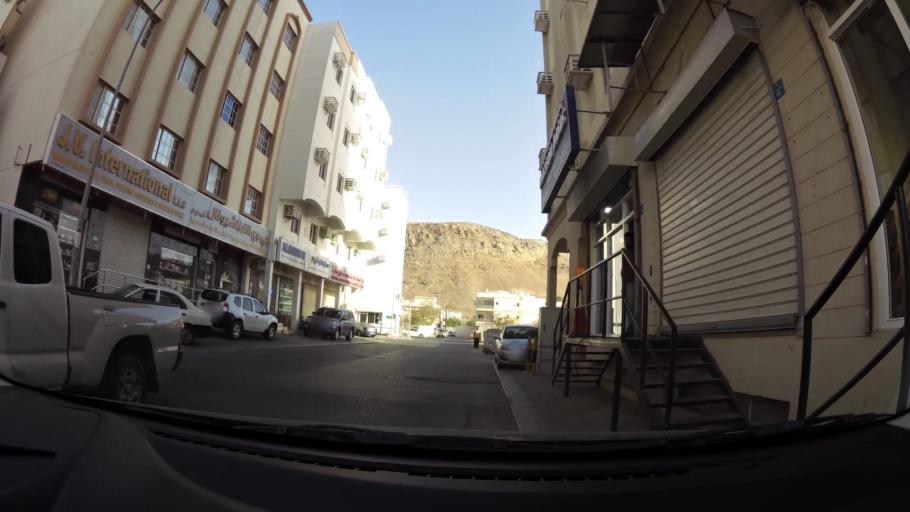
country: OM
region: Muhafazat Masqat
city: Muscat
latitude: 23.5860
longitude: 58.5498
